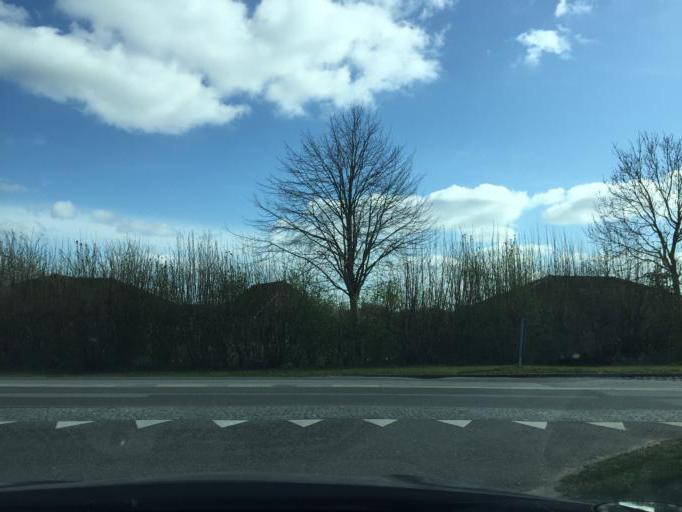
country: DK
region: South Denmark
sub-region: Faaborg-Midtfyn Kommune
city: Arslev
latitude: 55.3032
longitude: 10.4594
